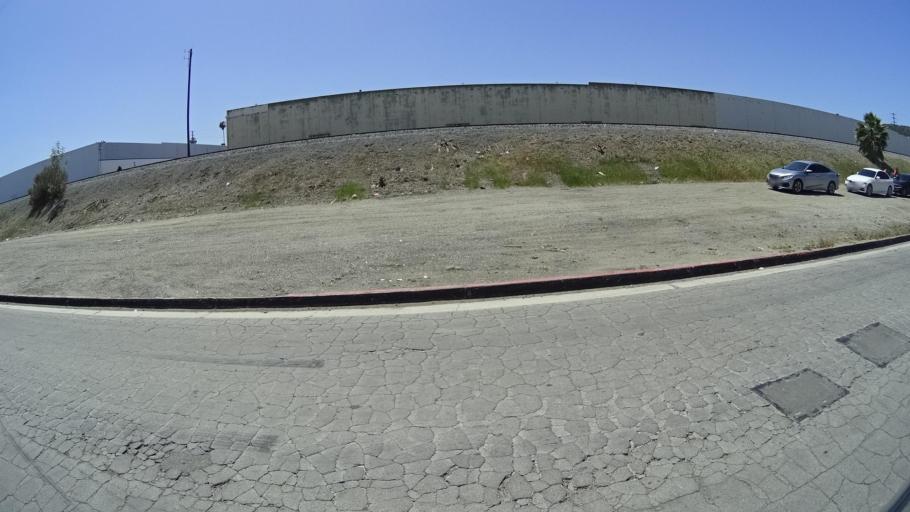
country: US
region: California
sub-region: Los Angeles County
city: Avocado Heights
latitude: 34.0237
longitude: -117.9830
